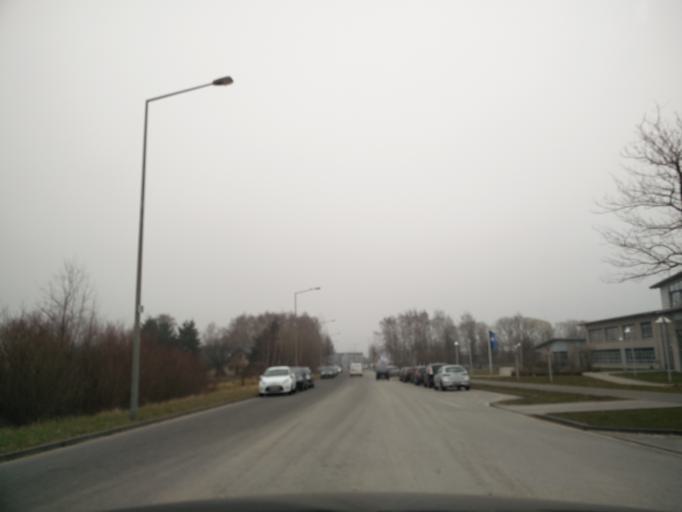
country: DE
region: North Rhine-Westphalia
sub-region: Regierungsbezirk Detmold
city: Paderborn
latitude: 51.7275
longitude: 8.7198
